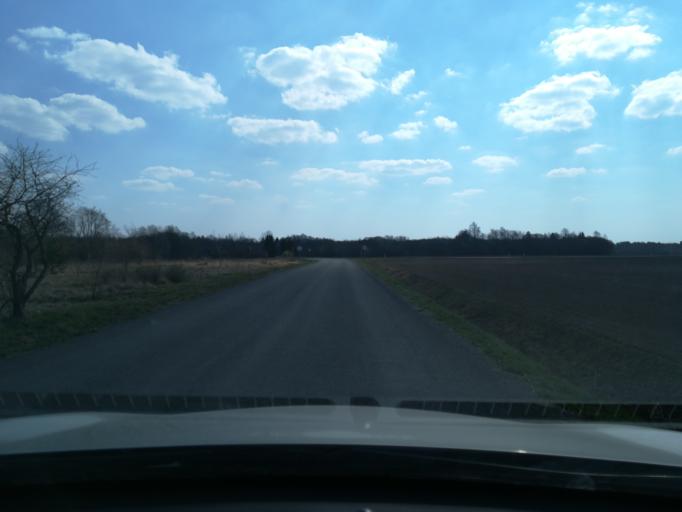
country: EE
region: Harju
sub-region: Saue linn
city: Saue
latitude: 59.3578
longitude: 24.5660
